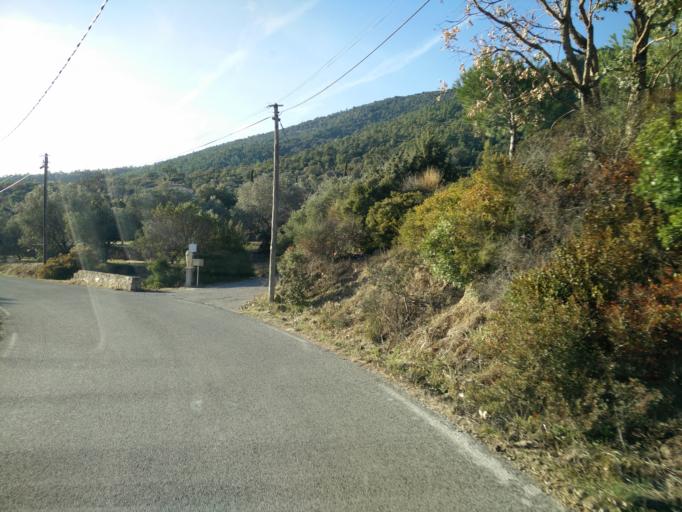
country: FR
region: Provence-Alpes-Cote d'Azur
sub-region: Departement du Var
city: Le Plan-de-la-Tour
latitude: 43.3421
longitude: 6.5300
